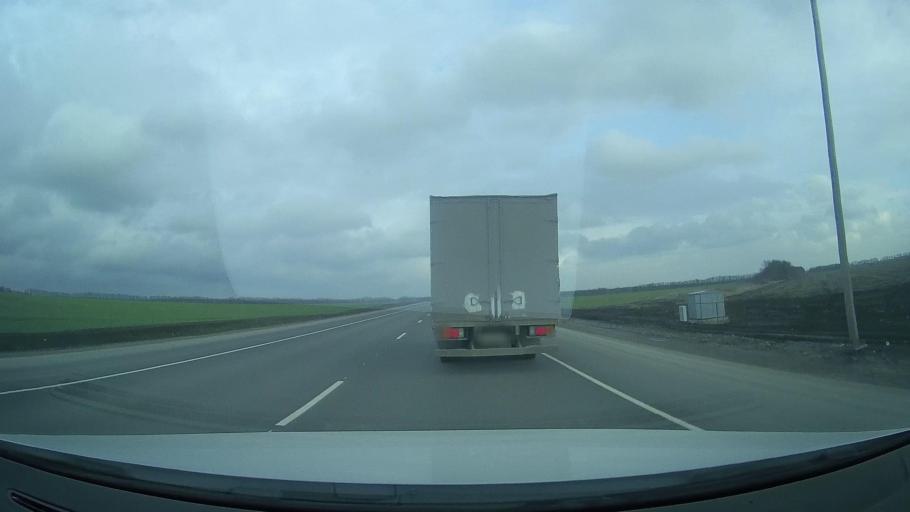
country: RU
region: Rostov
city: Grushevskaya
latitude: 47.4653
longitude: 39.8939
